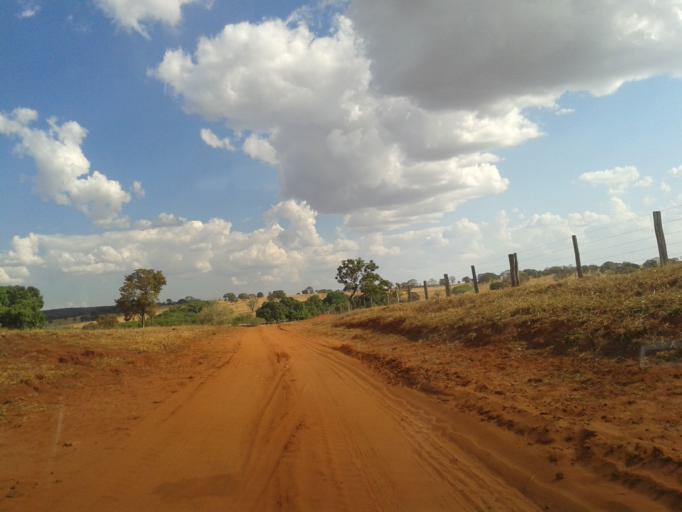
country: BR
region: Minas Gerais
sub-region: Santa Vitoria
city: Santa Vitoria
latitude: -19.2676
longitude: -49.9890
